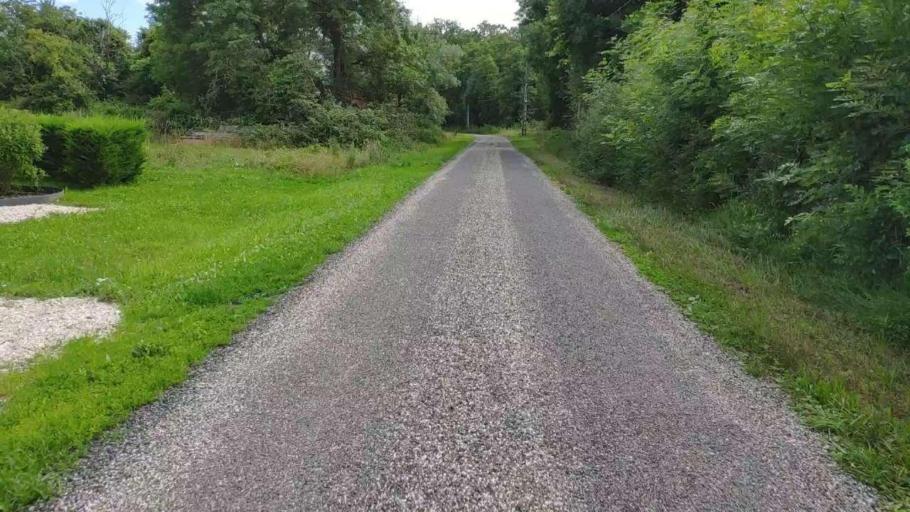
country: FR
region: Franche-Comte
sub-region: Departement du Jura
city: Bletterans
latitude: 46.8155
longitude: 5.4280
